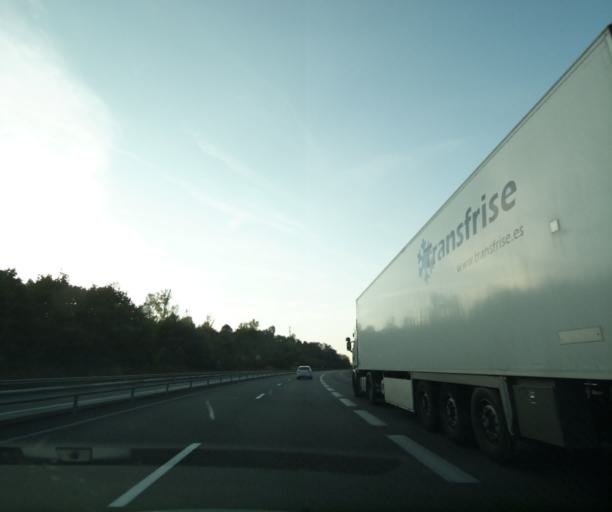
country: FR
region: Aquitaine
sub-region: Departement du Lot-et-Garonne
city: Boe
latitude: 44.1414
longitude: 0.6366
